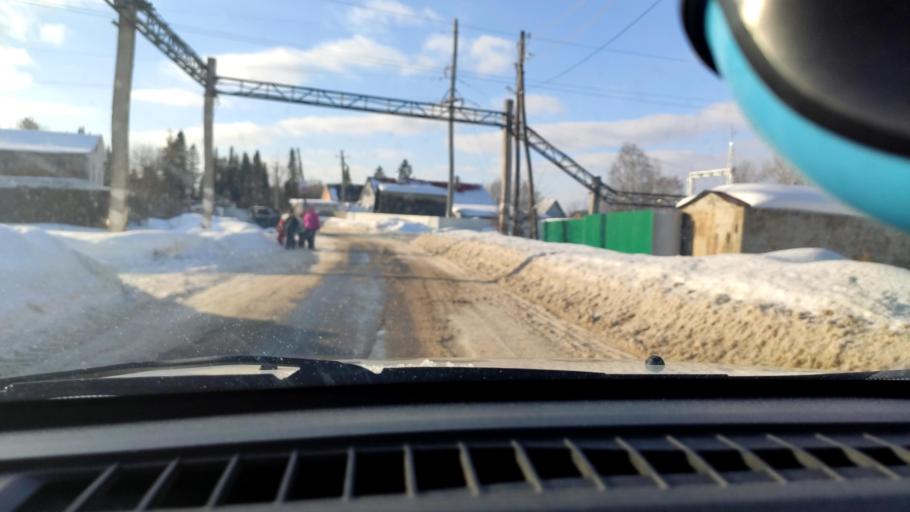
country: RU
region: Perm
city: Kultayevo
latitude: 57.9375
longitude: 55.8604
